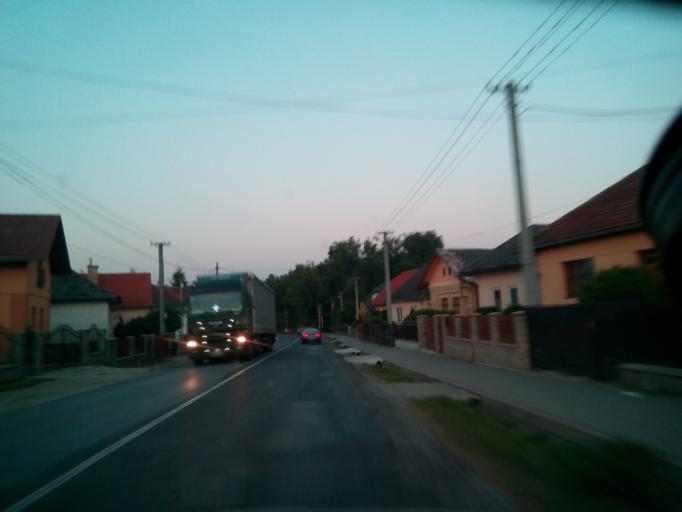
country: SK
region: Kosicky
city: Spisska Nova Ves
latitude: 48.9558
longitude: 20.5197
